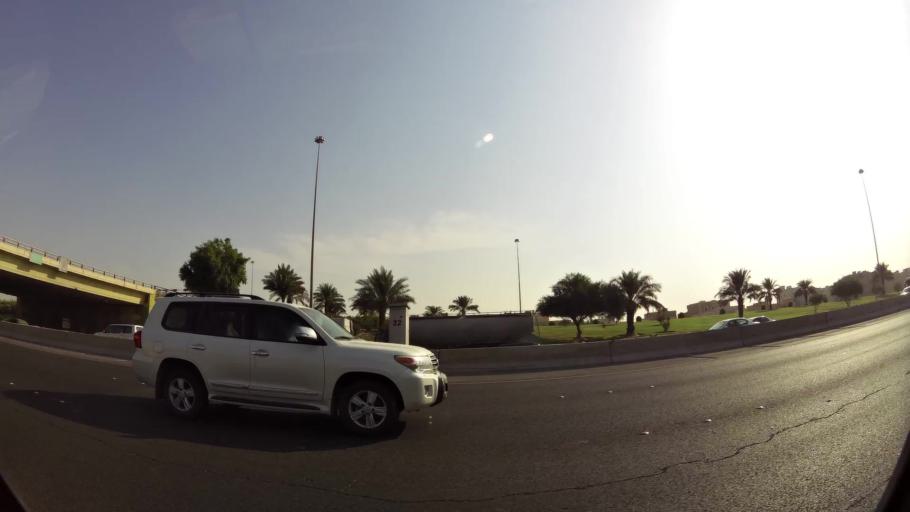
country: KW
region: Al Ahmadi
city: Ar Riqqah
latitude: 29.1301
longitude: 48.0915
